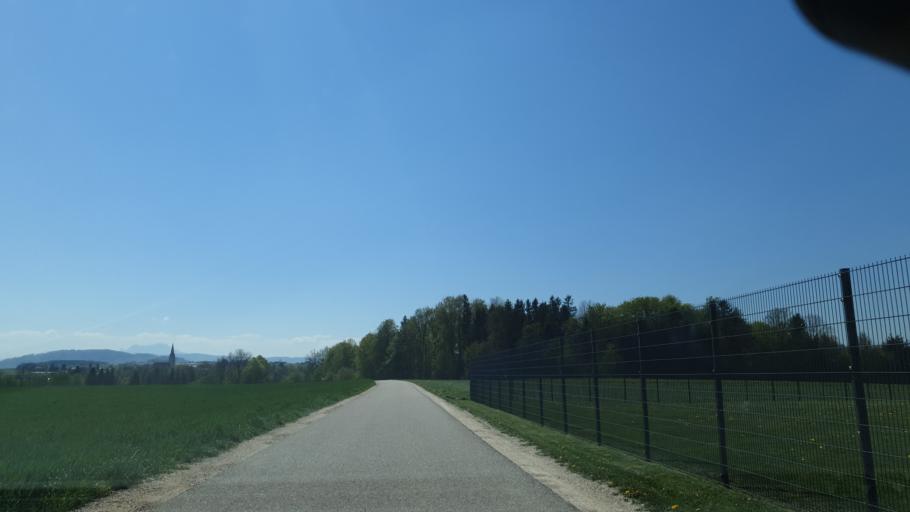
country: AT
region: Upper Austria
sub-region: Politischer Bezirk Vocklabruck
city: Gampern
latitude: 48.0007
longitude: 13.5620
